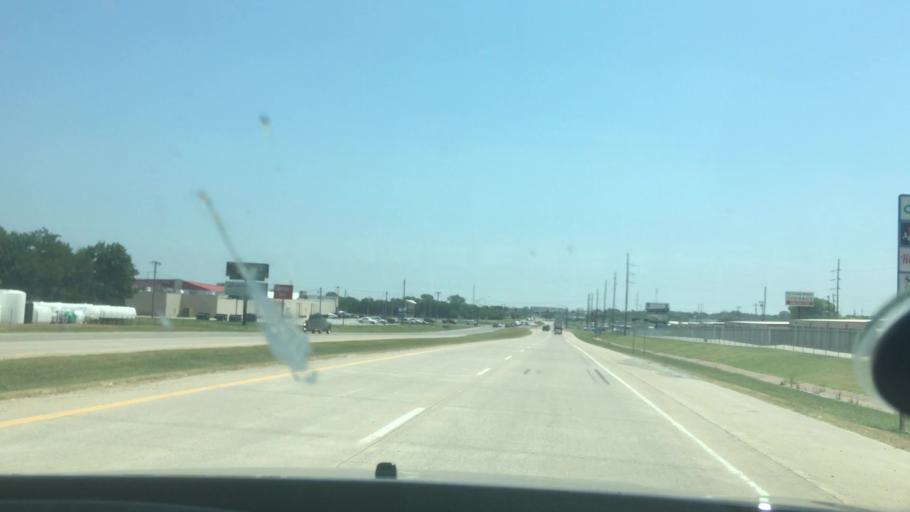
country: US
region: Oklahoma
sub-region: Pontotoc County
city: Ada
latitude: 34.7897
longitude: -96.6827
